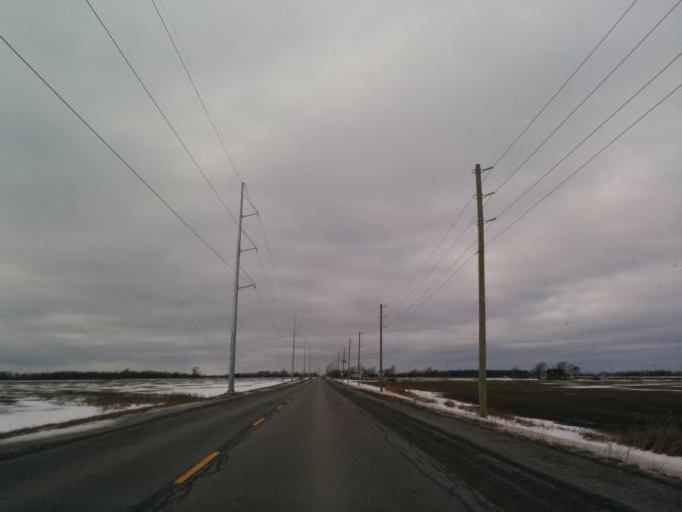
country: CA
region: Ontario
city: Ancaster
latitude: 42.9294
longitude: -79.9609
